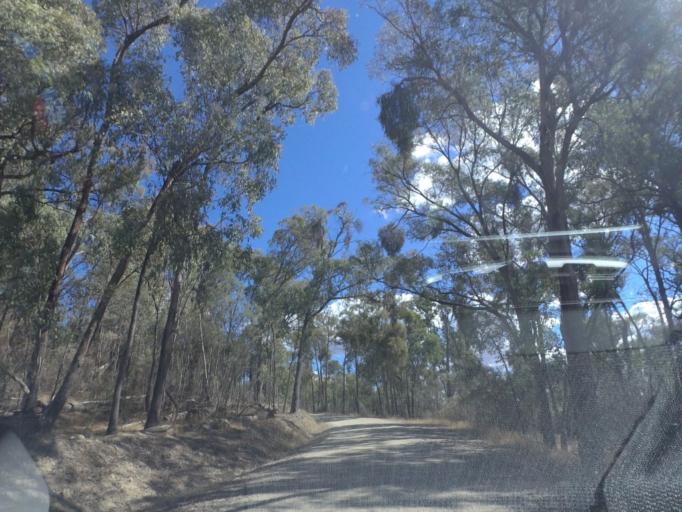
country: AU
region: Victoria
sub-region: Murrindindi
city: Alexandra
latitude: -37.3170
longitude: 145.8131
